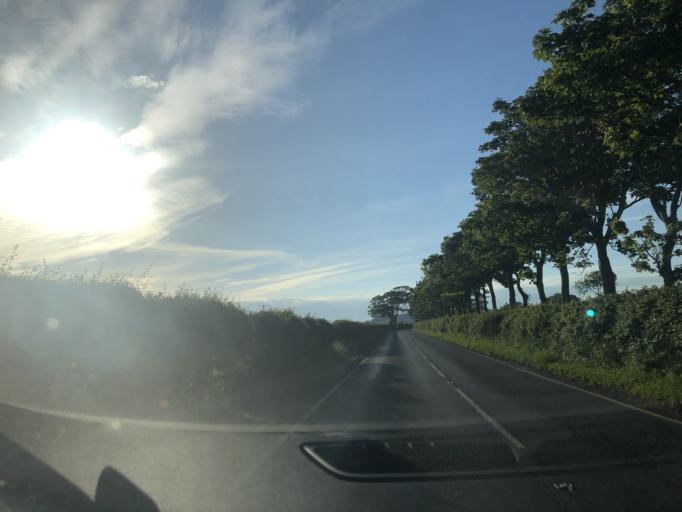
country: GB
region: Scotland
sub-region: Fife
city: Saint Monance
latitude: 56.1977
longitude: -2.8293
